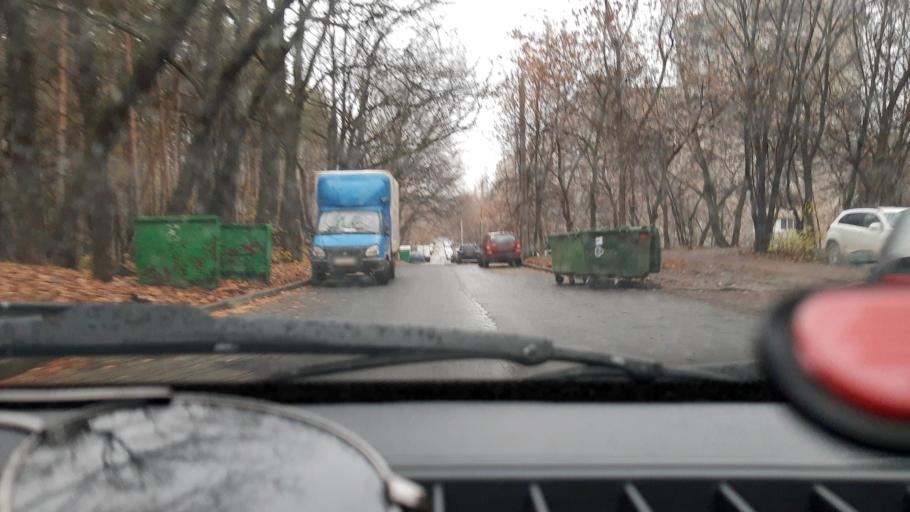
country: RU
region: Bashkortostan
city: Ufa
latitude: 54.7867
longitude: 56.0465
